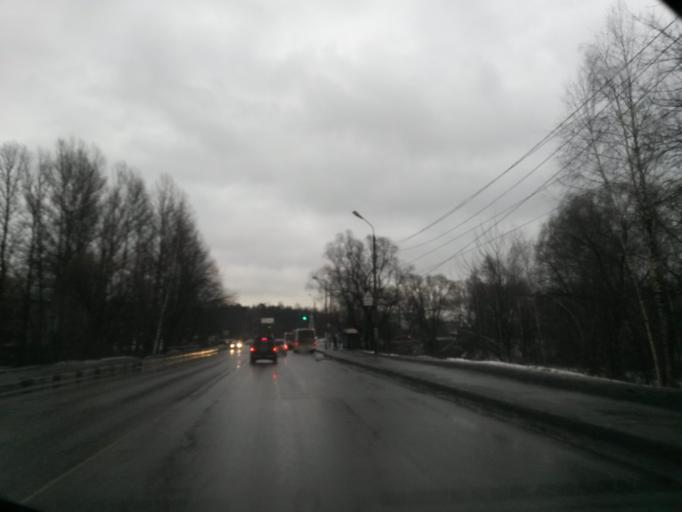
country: RU
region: Jaroslavl
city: Yaroslavl
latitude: 57.6440
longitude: 39.9153
